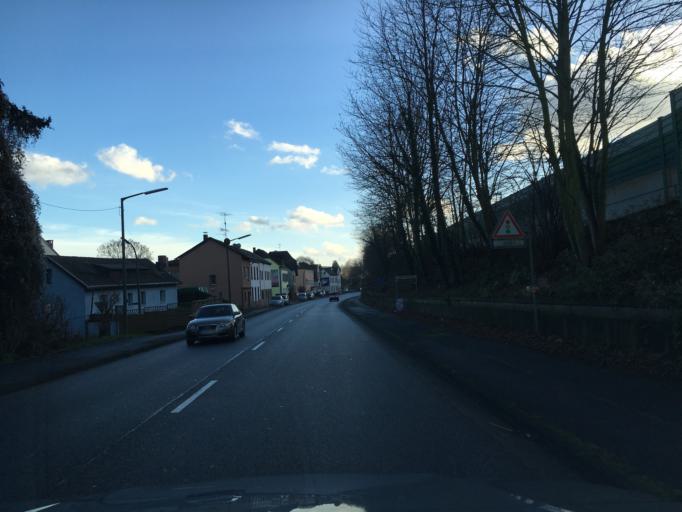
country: DE
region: North Rhine-Westphalia
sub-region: Regierungsbezirk Koln
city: Bad Honnef
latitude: 50.6457
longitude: 7.2037
